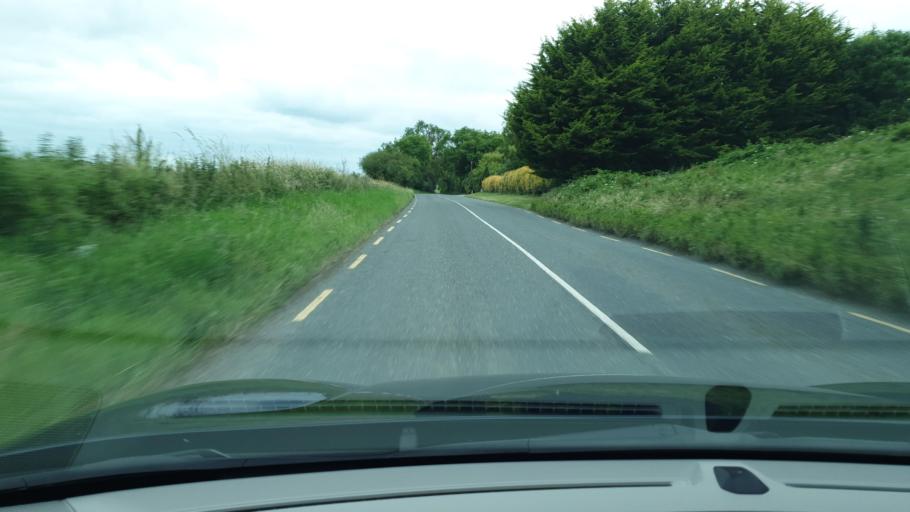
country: IE
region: Leinster
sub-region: An Mhi
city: Ashbourne
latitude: 53.4970
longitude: -6.4073
